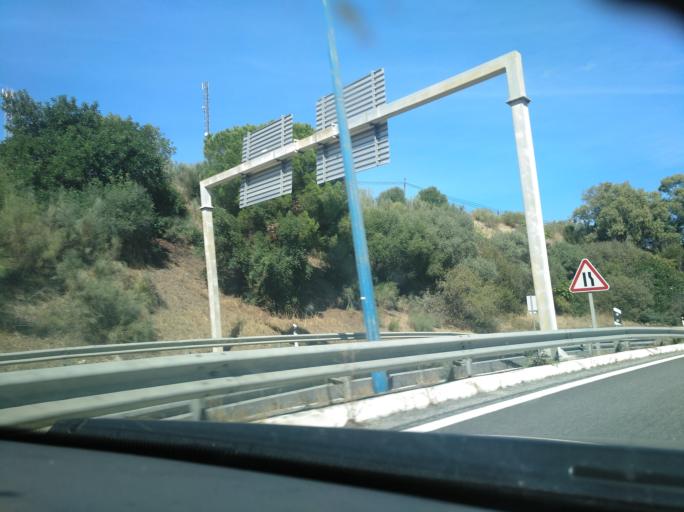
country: PT
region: Evora
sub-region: Arraiolos
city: Arraiolos
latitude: 38.7225
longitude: -7.9804
